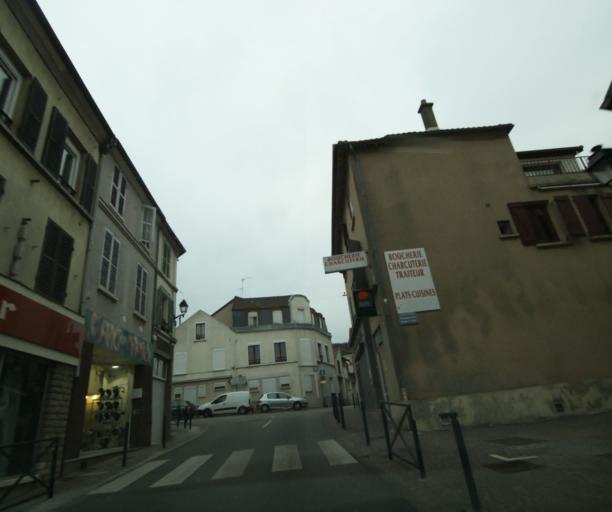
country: FR
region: Ile-de-France
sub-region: Departement des Yvelines
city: Chanteloup-les-Vignes
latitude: 48.9789
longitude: 2.0306
